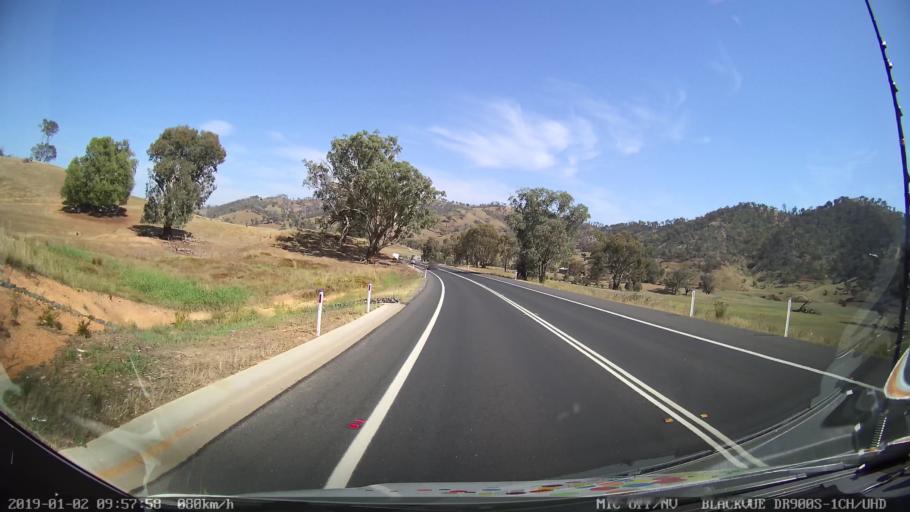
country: AU
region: New South Wales
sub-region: Tumut Shire
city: Tumut
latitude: -35.1994
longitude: 148.1641
